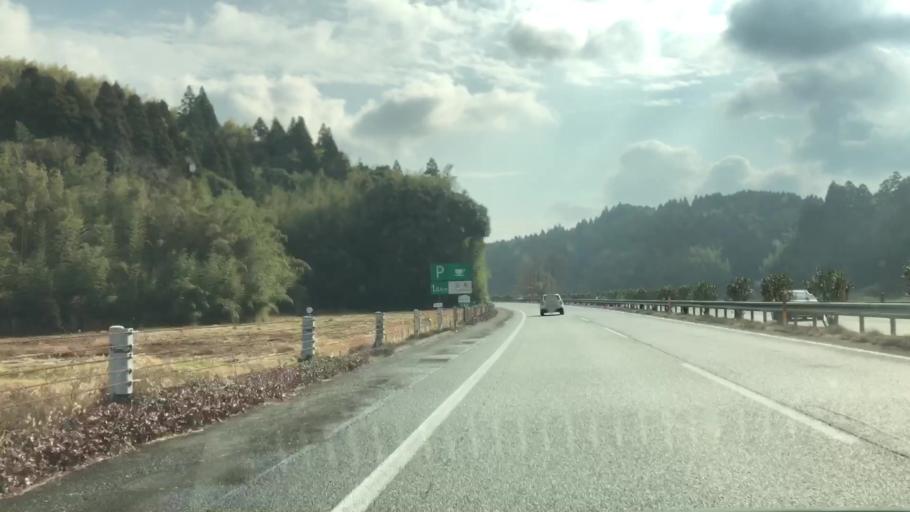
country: JP
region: Kumamoto
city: Yamaga
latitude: 33.0258
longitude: 130.5772
